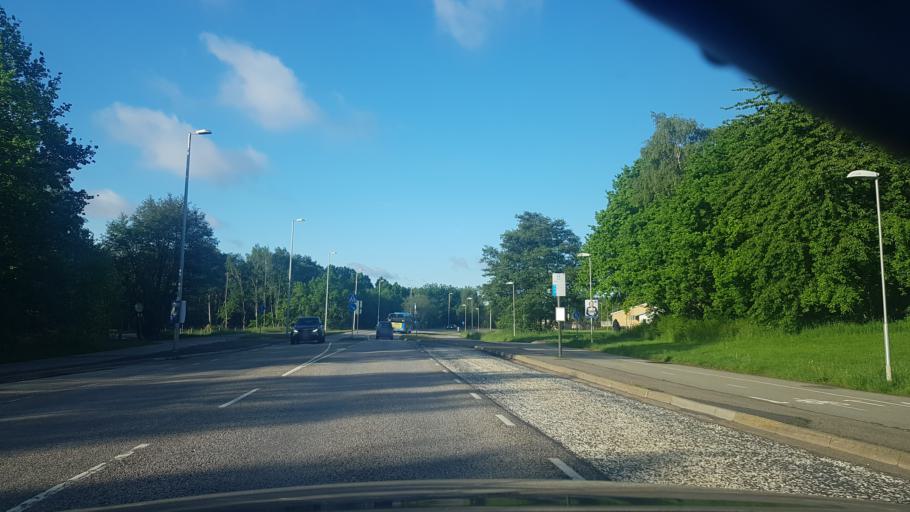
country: SE
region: Vaestra Goetaland
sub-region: Goteborg
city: Majorna
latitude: 57.6405
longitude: 11.9152
